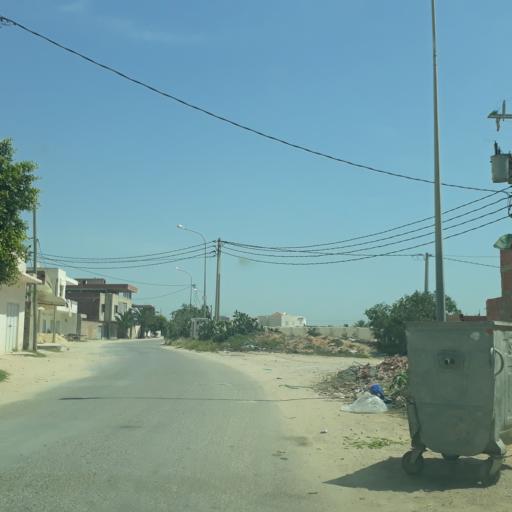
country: TN
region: Safaqis
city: Al Qarmadah
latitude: 34.8218
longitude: 10.7801
